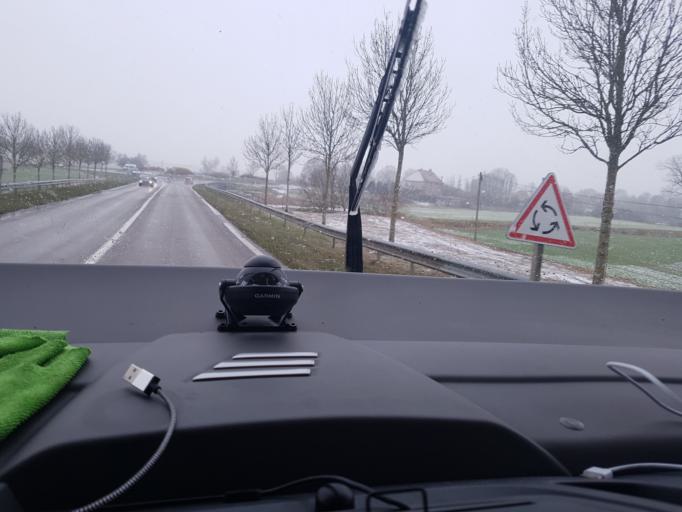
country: FR
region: Lorraine
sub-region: Departement de la Moselle
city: Vic-sur-Seille
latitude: 48.7834
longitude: 6.5677
